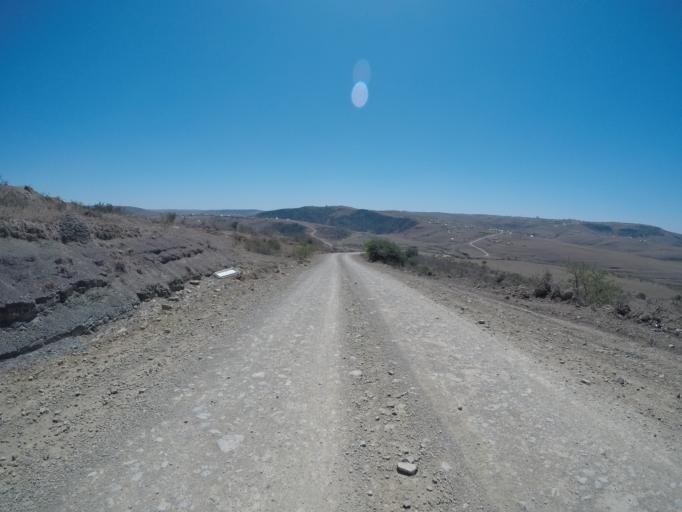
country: ZA
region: Eastern Cape
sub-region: OR Tambo District Municipality
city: Mthatha
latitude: -31.8761
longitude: 28.8730
